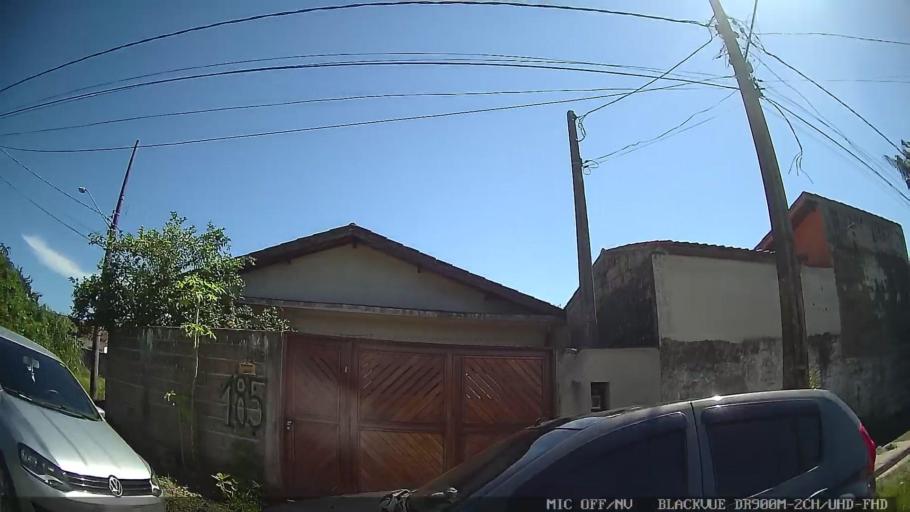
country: BR
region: Sao Paulo
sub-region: Iguape
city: Iguape
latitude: -24.6935
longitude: -47.5610
